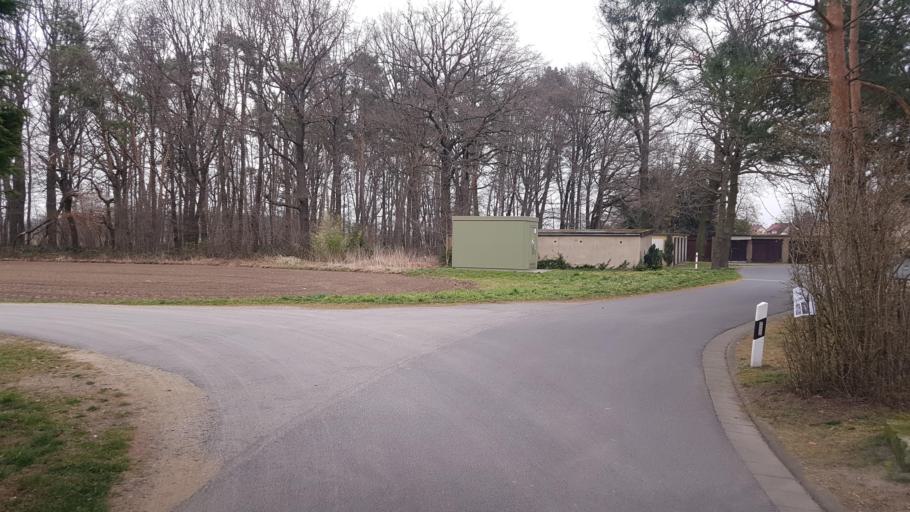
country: DE
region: Saxony
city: Nauwalde
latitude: 51.4224
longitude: 13.4503
